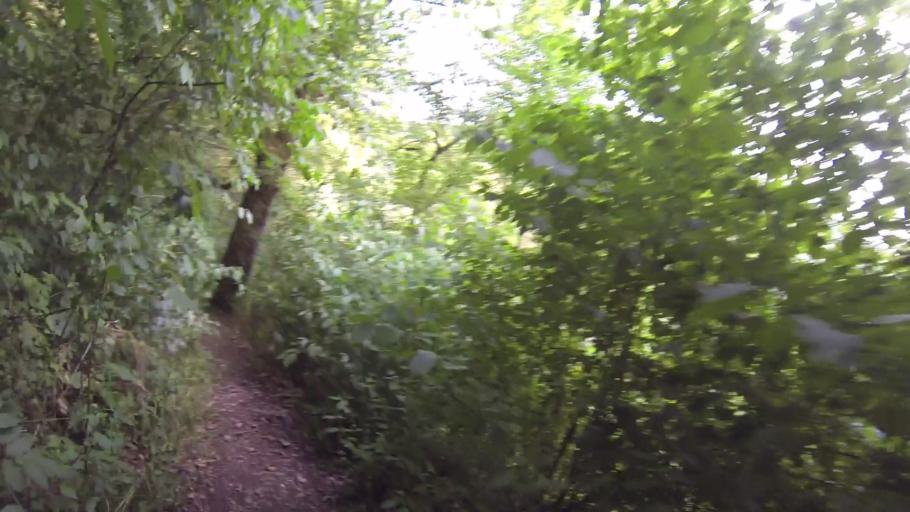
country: DE
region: Baden-Wuerttemberg
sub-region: Tuebingen Region
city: Blaubeuren
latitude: 48.4503
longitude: 9.8591
